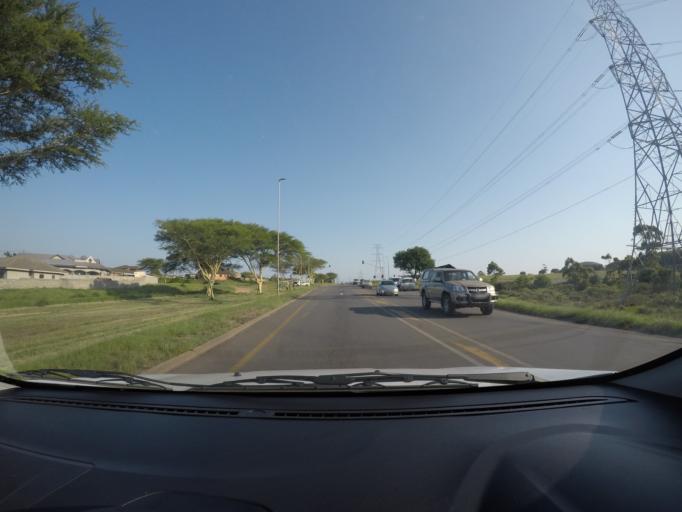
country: ZA
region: KwaZulu-Natal
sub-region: uThungulu District Municipality
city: Richards Bay
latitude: -28.7246
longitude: 32.0351
